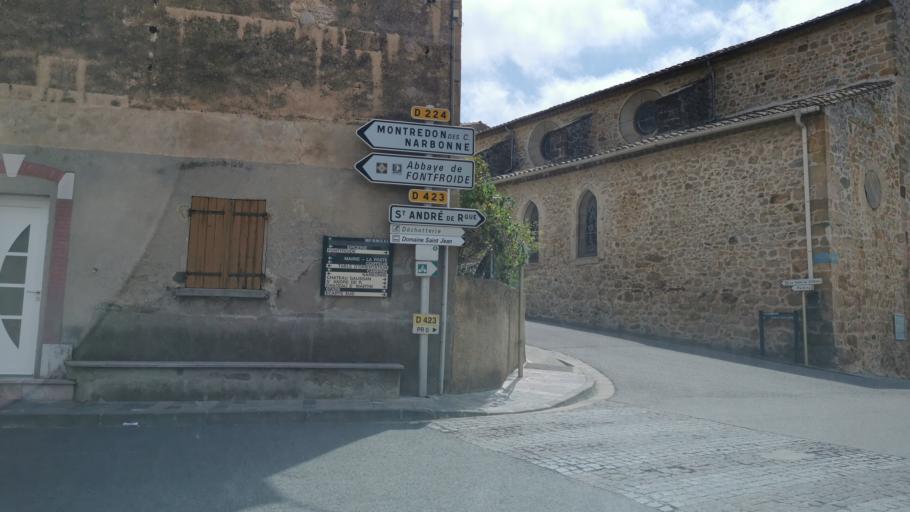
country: FR
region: Languedoc-Roussillon
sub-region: Departement de l'Aude
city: Bizanet
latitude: 43.1639
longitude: 2.8699
